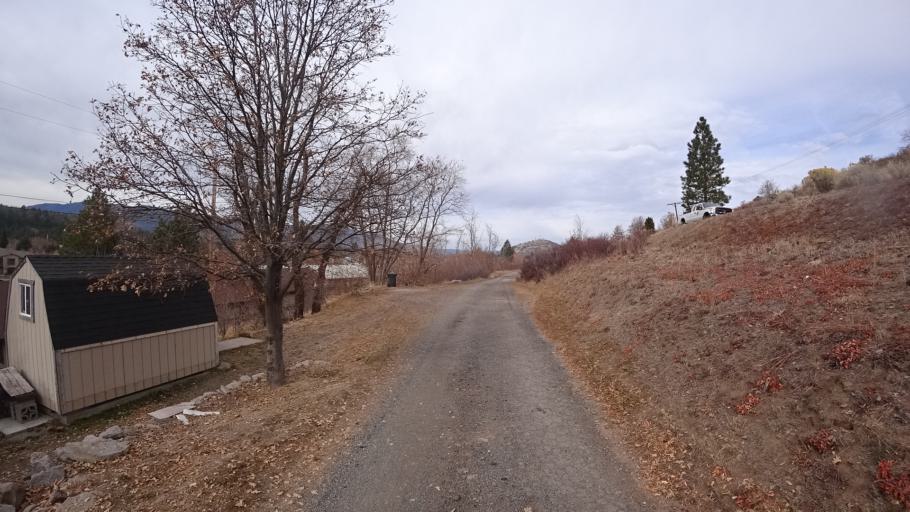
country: US
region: California
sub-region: Siskiyou County
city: Weed
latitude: 41.4230
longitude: -122.3804
